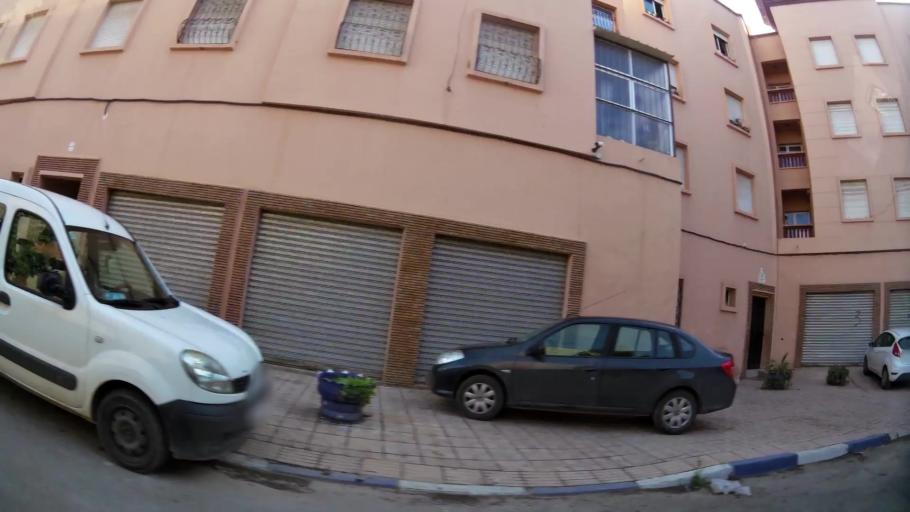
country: MA
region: Marrakech-Tensift-Al Haouz
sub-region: Marrakech
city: Marrakesh
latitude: 31.6896
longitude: -8.0739
